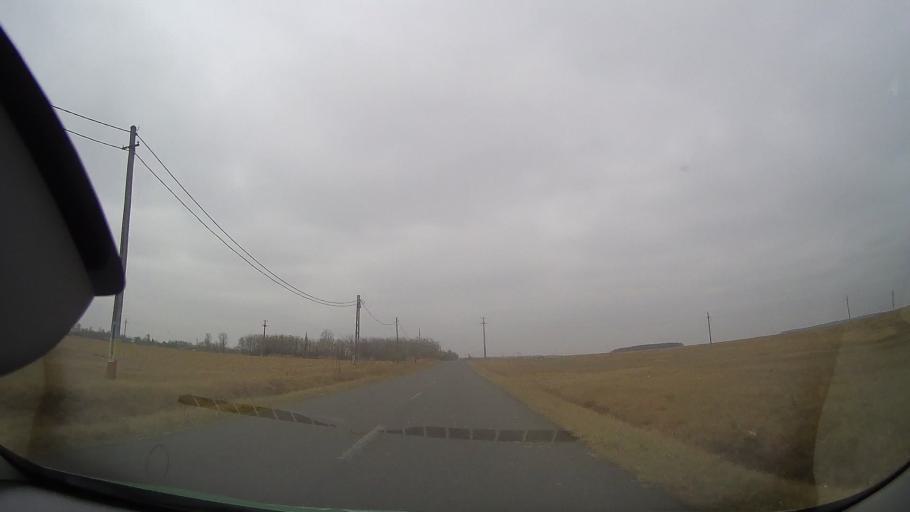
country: RO
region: Buzau
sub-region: Comuna Scutelnici
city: Scutelnici
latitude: 44.8512
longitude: 26.9120
